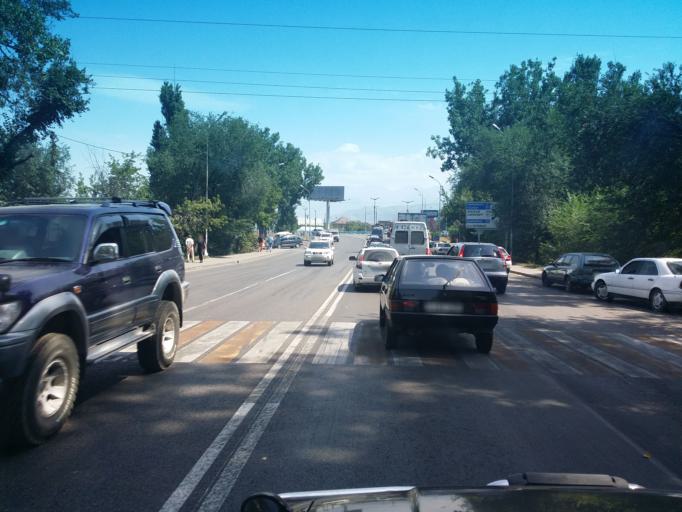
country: KZ
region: Almaty Oblysy
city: Pervomayskiy
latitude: 43.3412
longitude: 76.9815
